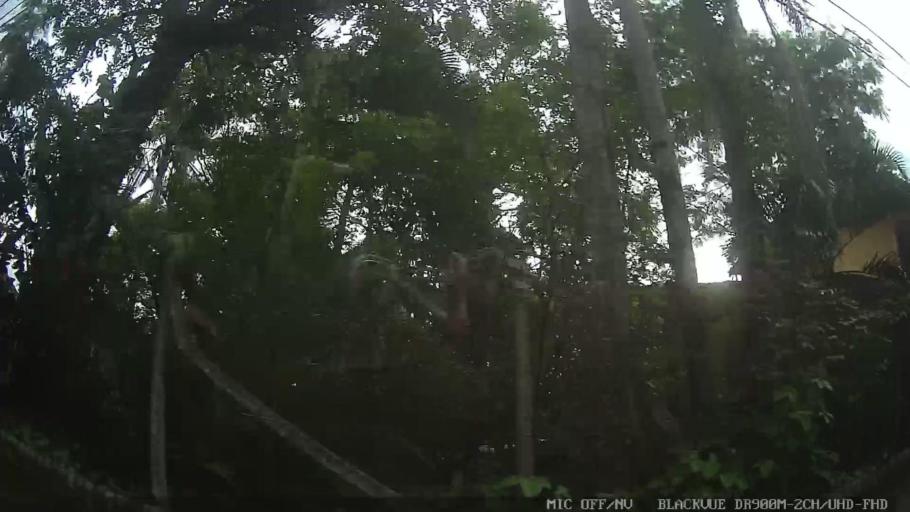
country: BR
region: Sao Paulo
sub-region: Atibaia
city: Atibaia
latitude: -23.1176
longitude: -46.5460
